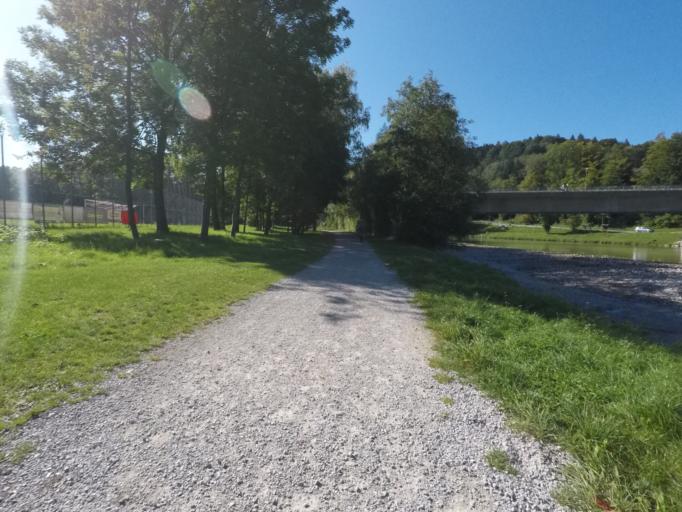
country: DE
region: Bavaria
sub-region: Upper Bavaria
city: Bad Toelz
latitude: 47.7551
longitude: 11.5571
